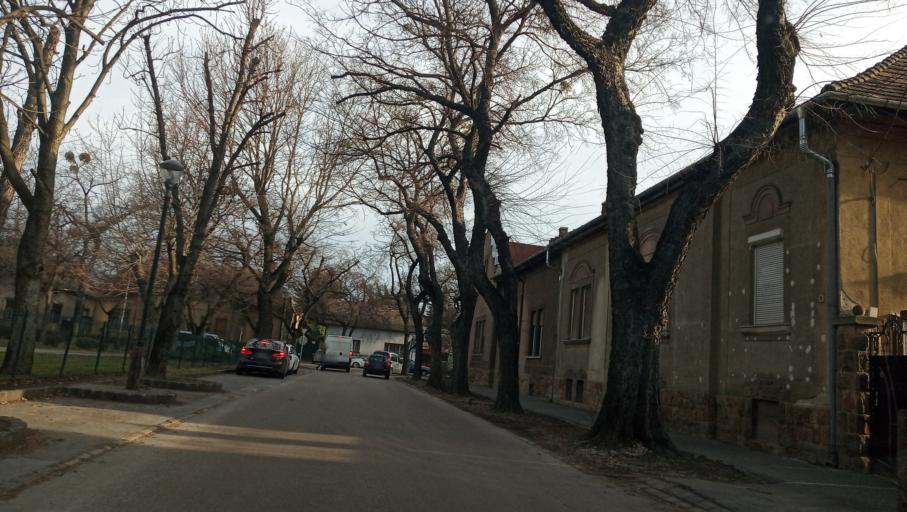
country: HU
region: Pest
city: Vac
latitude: 47.7792
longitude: 19.1319
